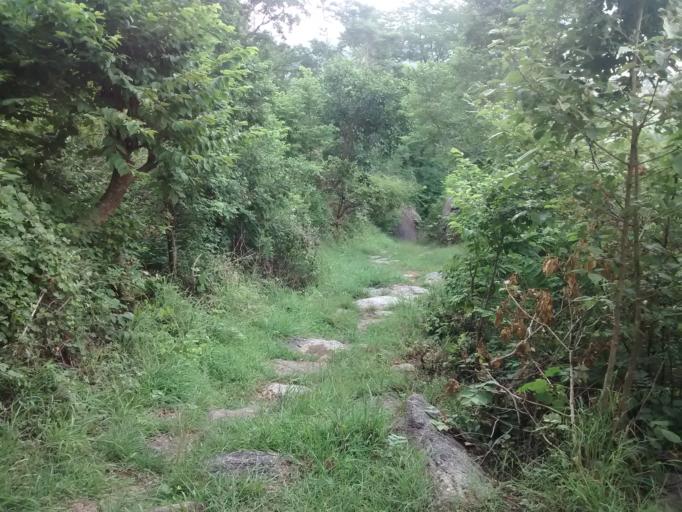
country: IN
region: Karnataka
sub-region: Tumkur
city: Tumkur
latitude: 13.3785
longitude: 77.2073
